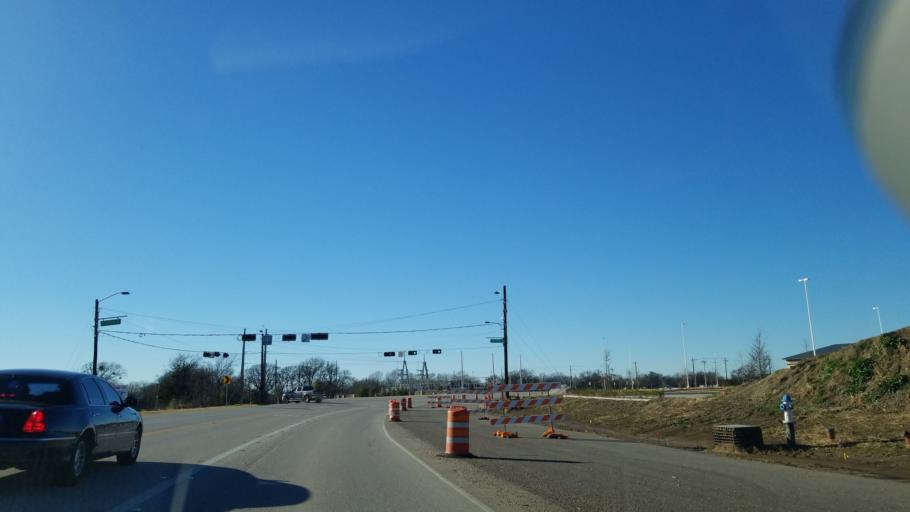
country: US
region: Texas
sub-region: Denton County
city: Copper Canyon
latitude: 33.1323
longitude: -97.1016
